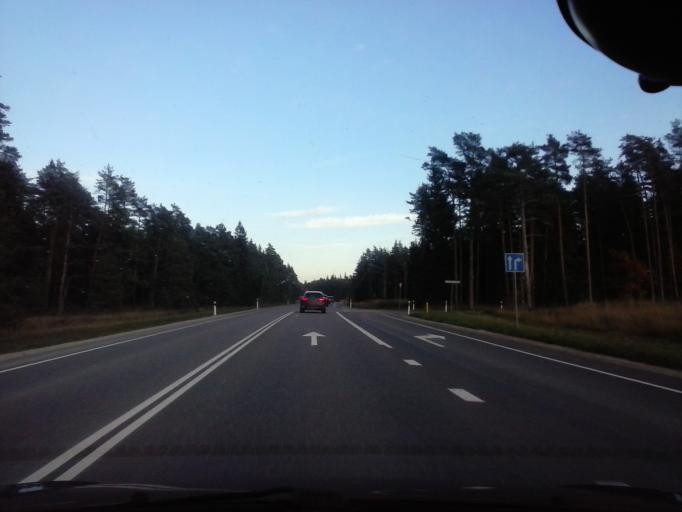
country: EE
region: Laeaene
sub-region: Lihula vald
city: Lihula
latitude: 58.9739
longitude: 23.9267
